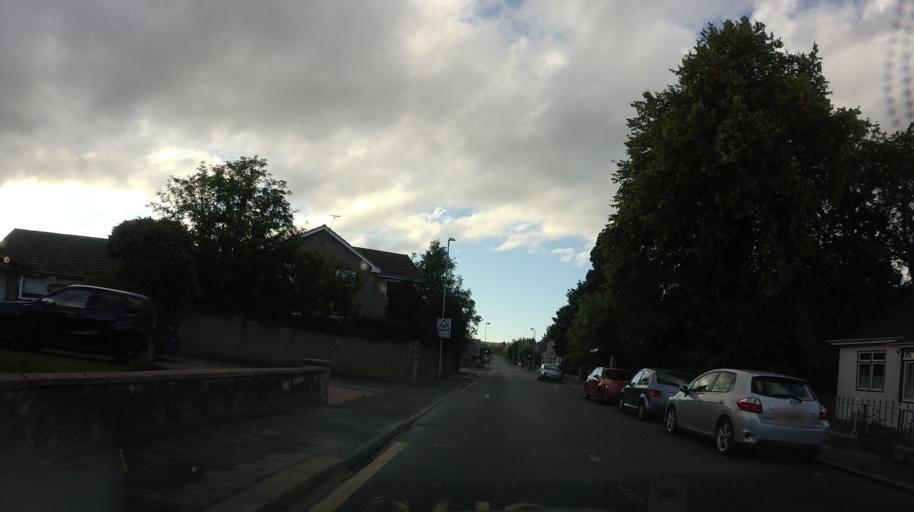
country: GB
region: Scotland
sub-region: Aberdeenshire
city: Alford
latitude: 57.2327
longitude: -2.7033
